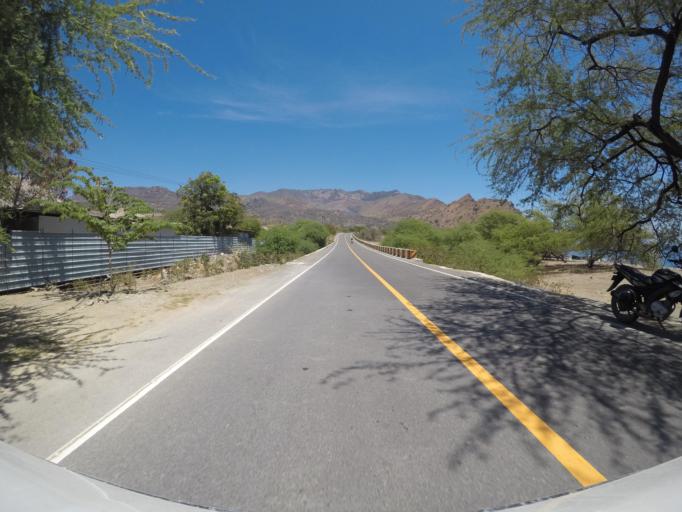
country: TL
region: Manatuto
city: Manatuto
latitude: -8.4884
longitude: 125.9746
